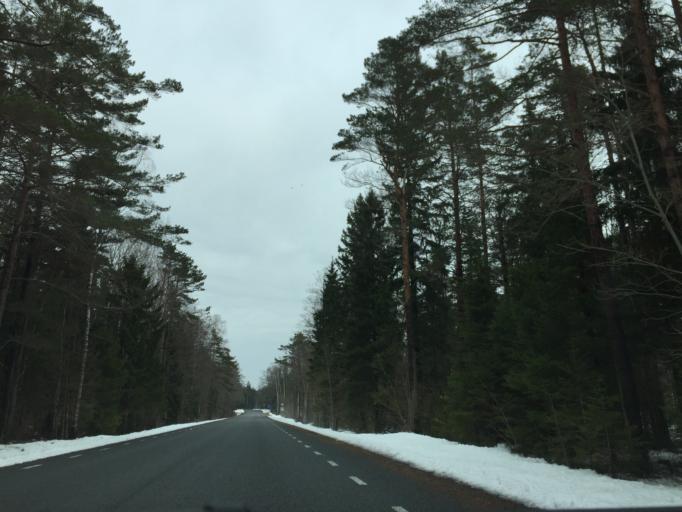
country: EE
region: Saare
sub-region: Kuressaare linn
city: Kuressaare
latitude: 58.4444
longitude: 22.2388
